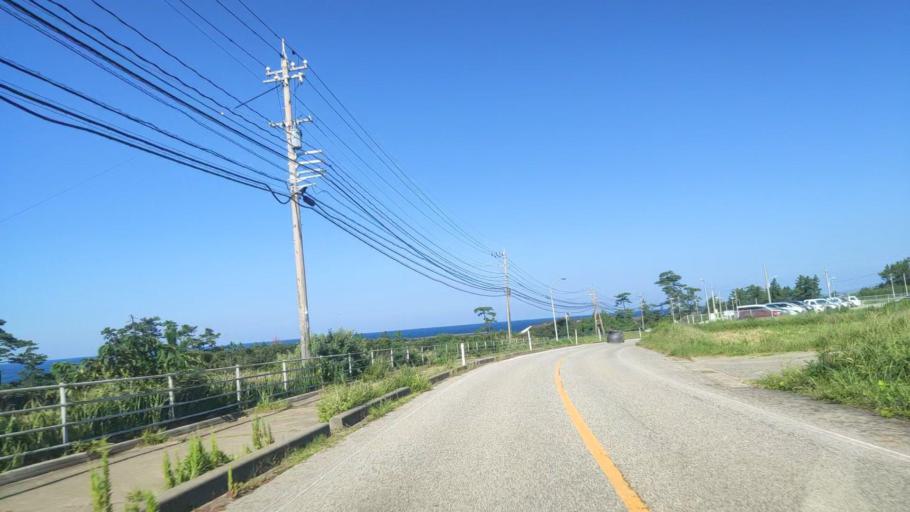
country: JP
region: Ishikawa
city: Hakui
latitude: 37.0537
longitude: 136.7268
